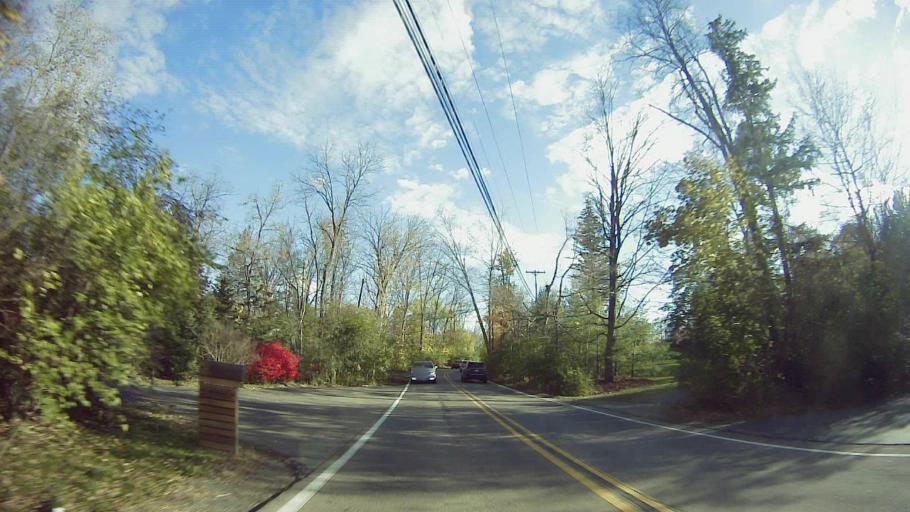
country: US
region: Michigan
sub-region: Oakland County
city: Beverly Hills
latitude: 42.5237
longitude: -83.2440
